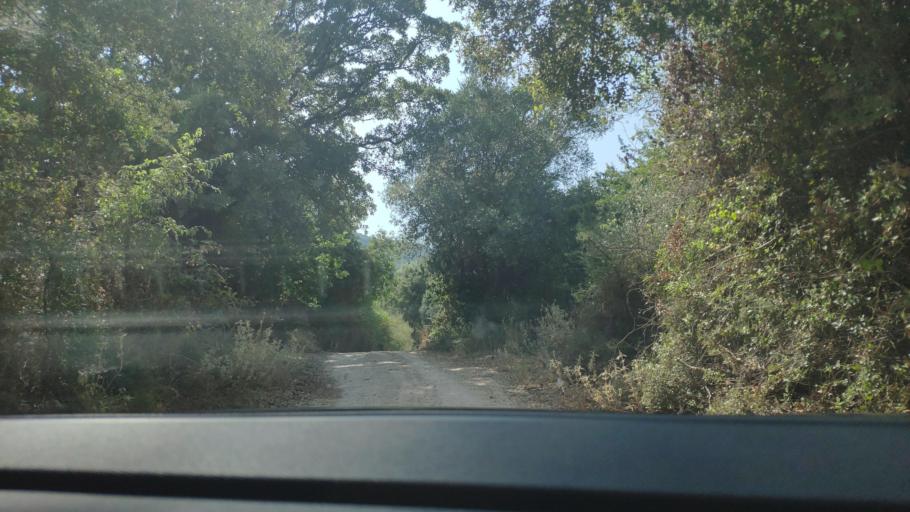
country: GR
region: West Greece
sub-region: Nomos Aitolias kai Akarnanias
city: Fitiai
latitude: 38.7174
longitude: 21.1961
